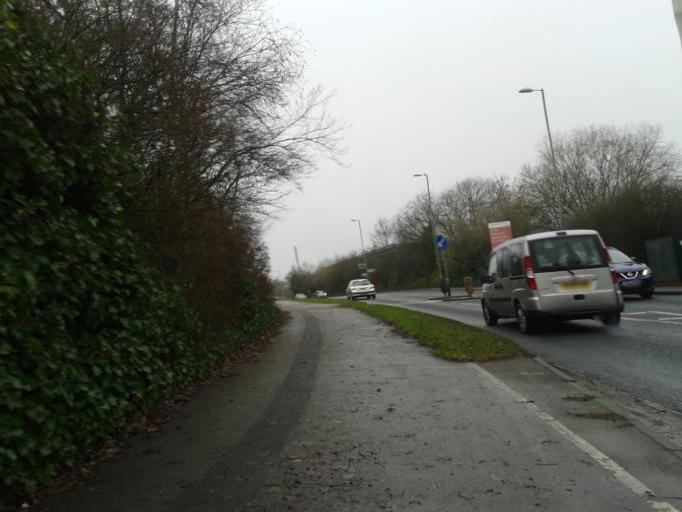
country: GB
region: England
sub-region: Hampshire
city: Farnborough
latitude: 51.2923
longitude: -0.7875
